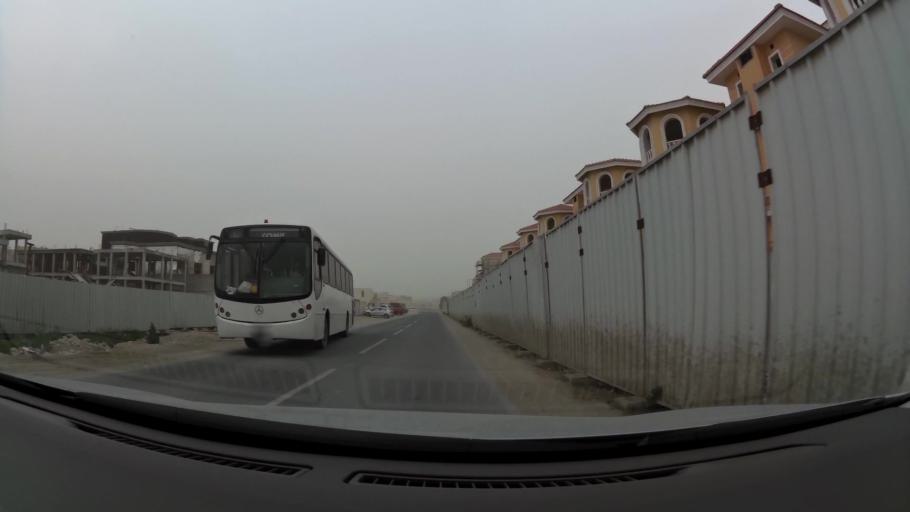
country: QA
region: Baladiyat ad Dawhah
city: Doha
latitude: 25.2457
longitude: 51.4863
